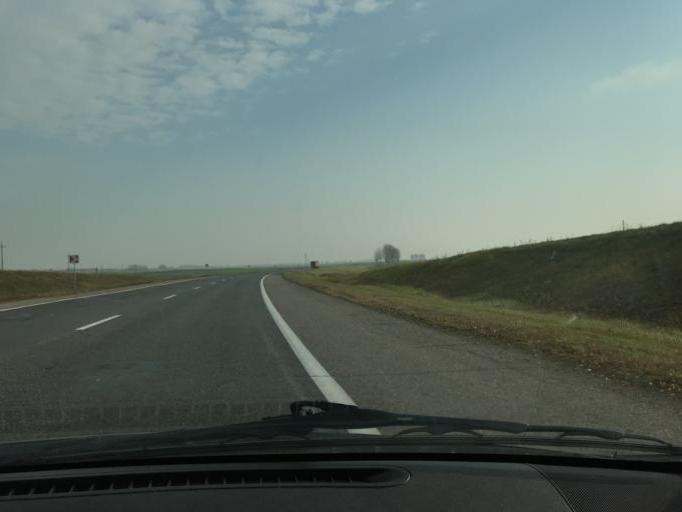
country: BY
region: Vitebsk
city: Chashniki
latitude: 55.0174
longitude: 29.0347
